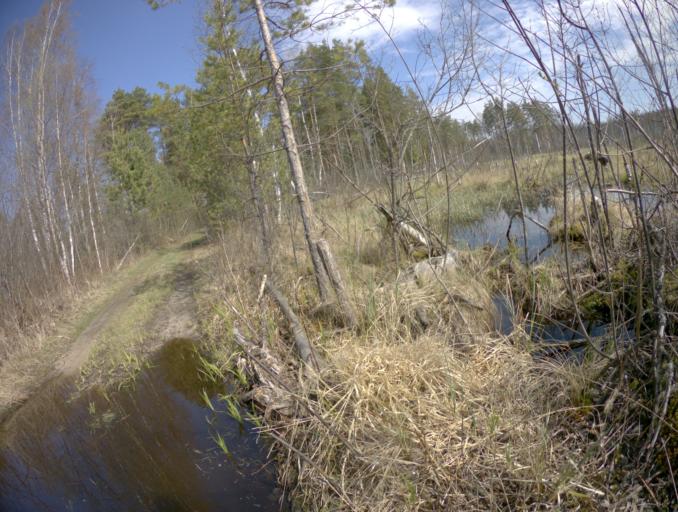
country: RU
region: Vladimir
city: Mezinovskiy
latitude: 55.5272
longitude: 40.2591
